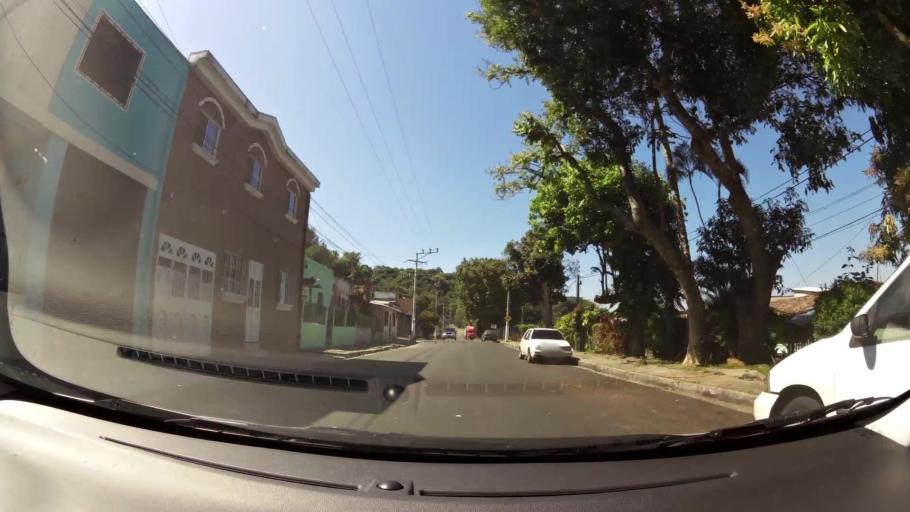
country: SV
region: La Libertad
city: Santa Tecla
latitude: 13.6727
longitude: -89.3014
